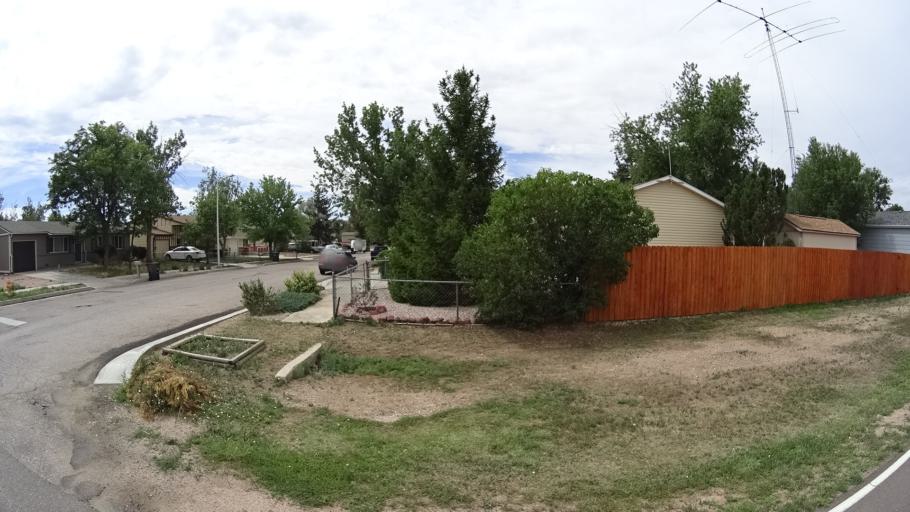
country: US
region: Colorado
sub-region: El Paso County
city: Fountain
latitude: 38.7084
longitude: -104.7001
